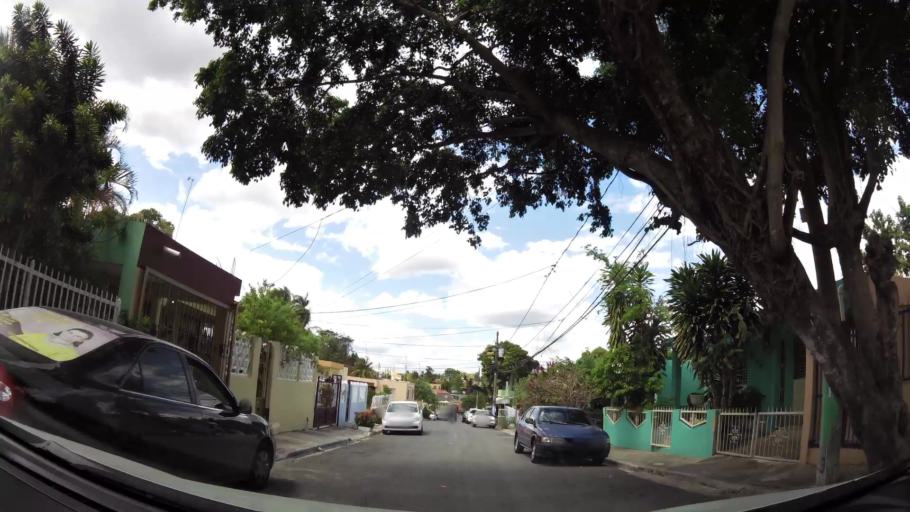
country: DO
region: Nacional
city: Ensanche Luperon
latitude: 18.5252
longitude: -69.8994
